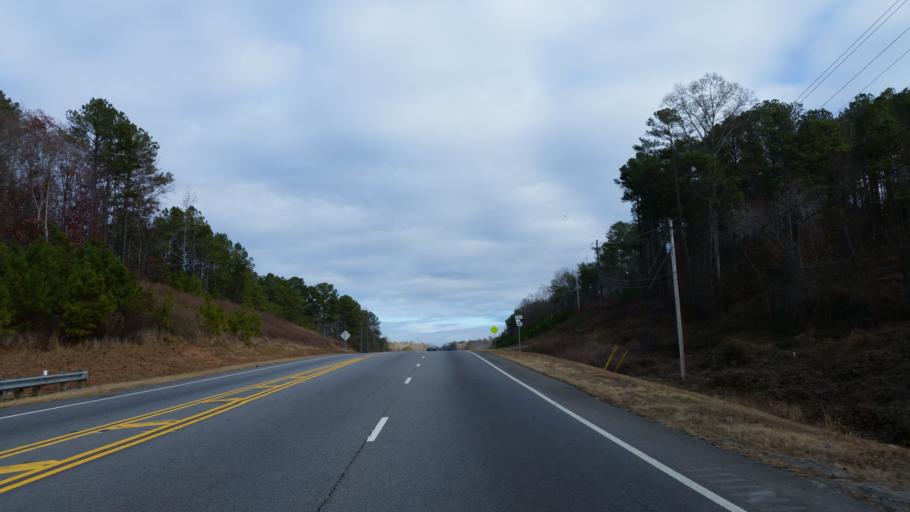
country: US
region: Georgia
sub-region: Bartow County
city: Cartersville
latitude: 34.2199
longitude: -84.7296
